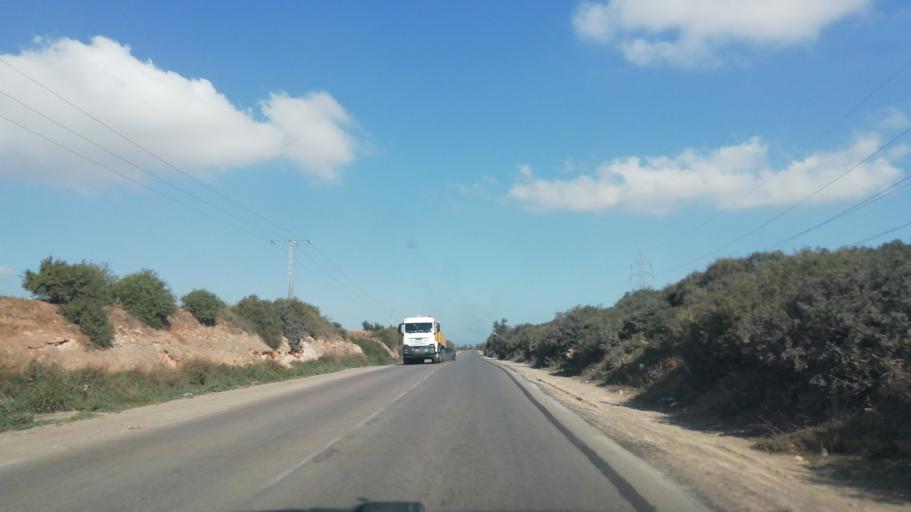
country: DZ
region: Oran
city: Ain el Bya
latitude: 35.7641
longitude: -0.2760
